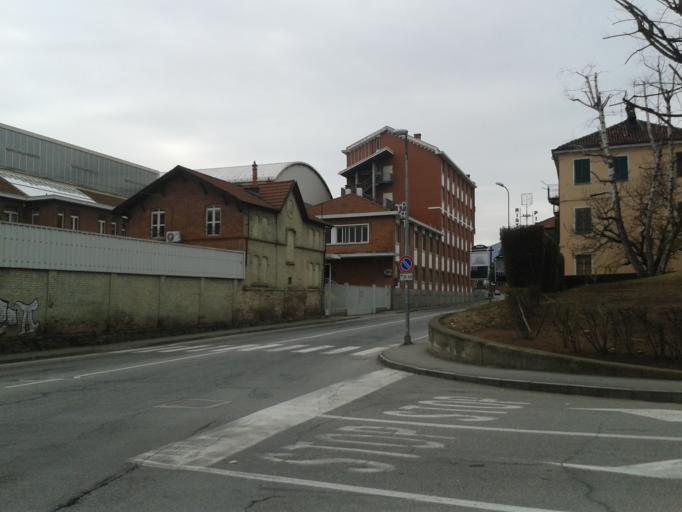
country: IT
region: Piedmont
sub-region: Provincia di Torino
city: Pinerolo
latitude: 44.8907
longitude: 7.3421
